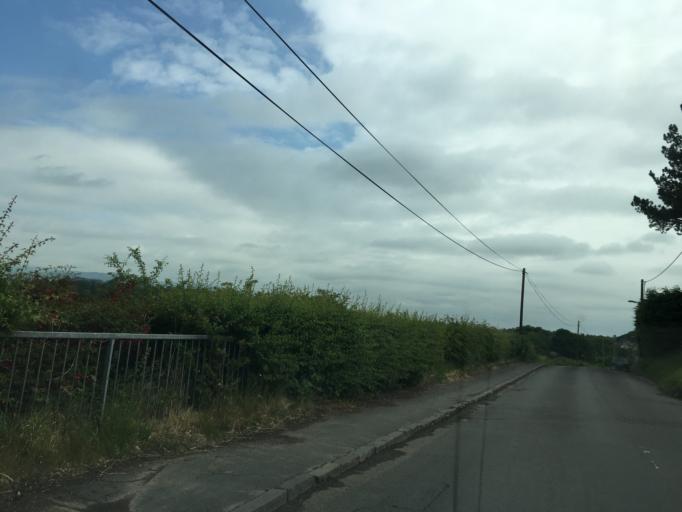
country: GB
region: Scotland
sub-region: Stirling
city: Stirling
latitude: 56.1097
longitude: -3.9757
